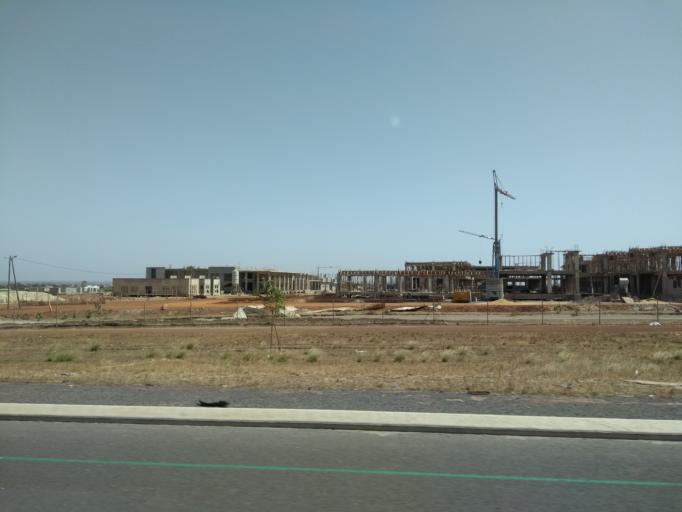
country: SN
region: Thies
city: Thies
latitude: 14.7364
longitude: -17.1969
